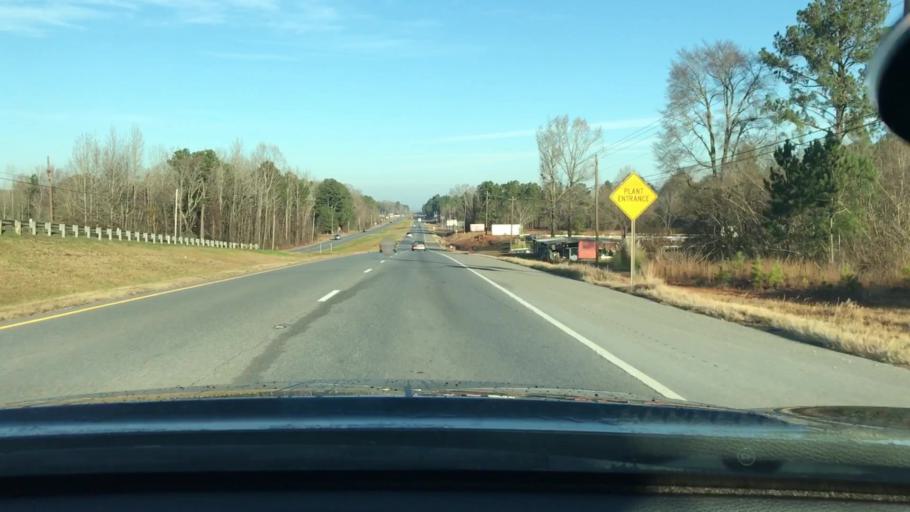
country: US
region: Alabama
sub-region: Talladega County
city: Childersburg
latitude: 33.2305
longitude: -86.3262
